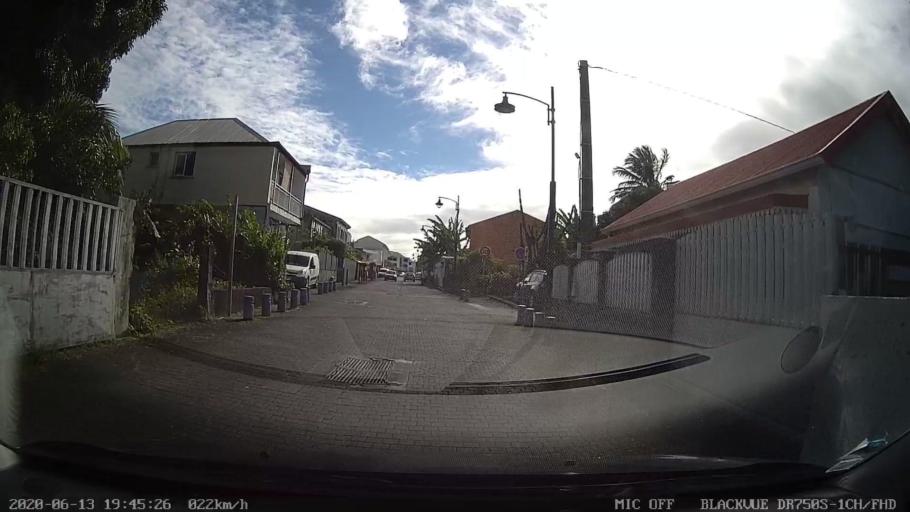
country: RE
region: Reunion
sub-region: Reunion
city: Bras-Panon
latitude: -20.9973
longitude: 55.6770
